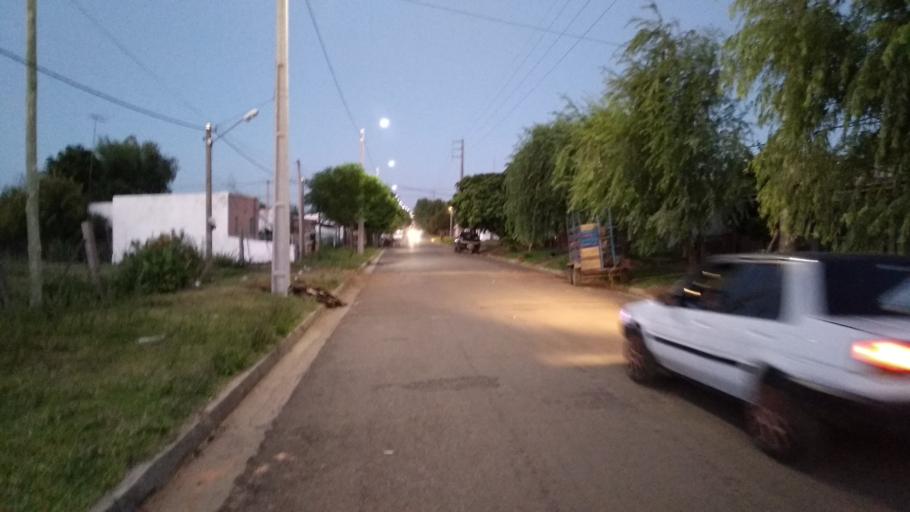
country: UY
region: Artigas
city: Artigas
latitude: -30.4100
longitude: -56.4834
